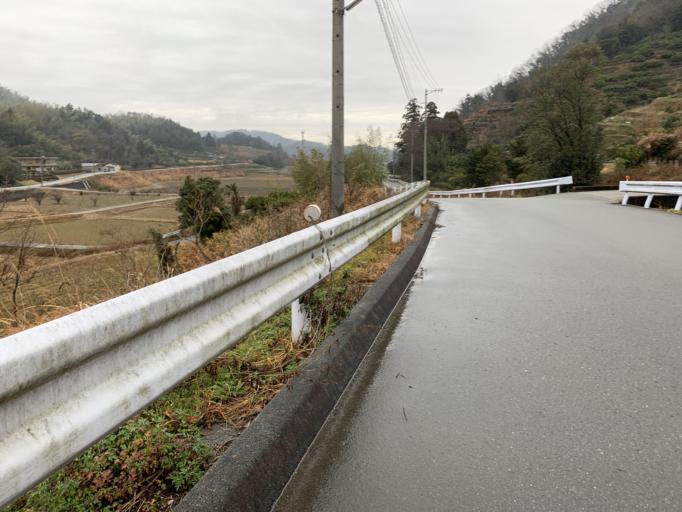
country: JP
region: Mie
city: Ise
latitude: 34.4701
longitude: 136.5476
